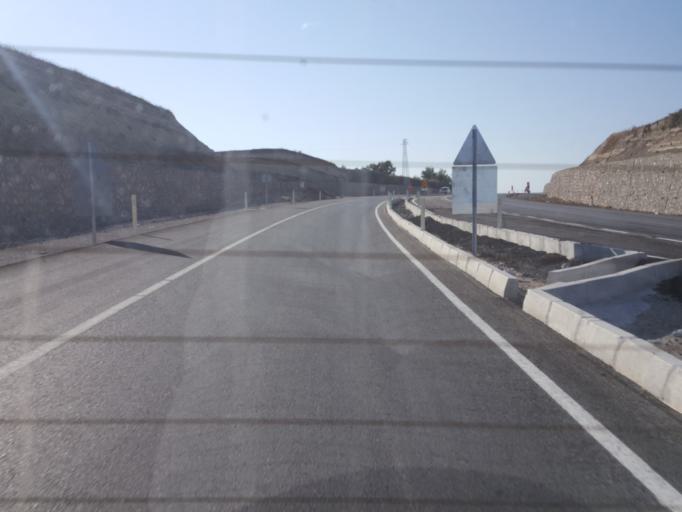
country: TR
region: Corum
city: Seydim
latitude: 40.5867
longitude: 34.7510
